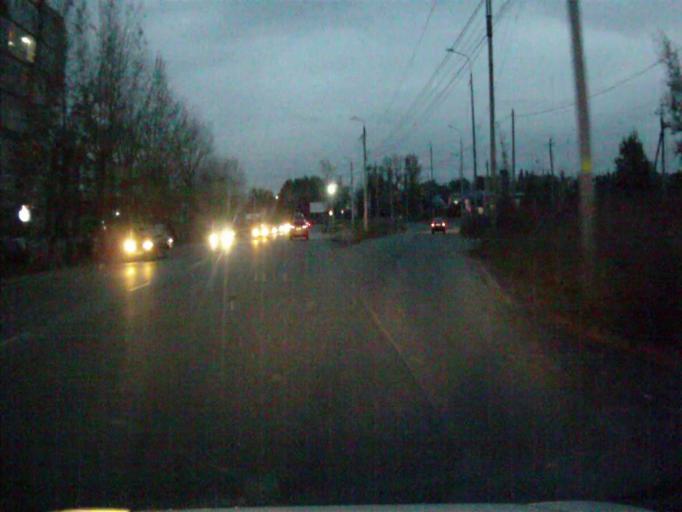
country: RU
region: Chelyabinsk
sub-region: Gorod Chelyabinsk
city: Chelyabinsk
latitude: 55.1584
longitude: 61.2977
